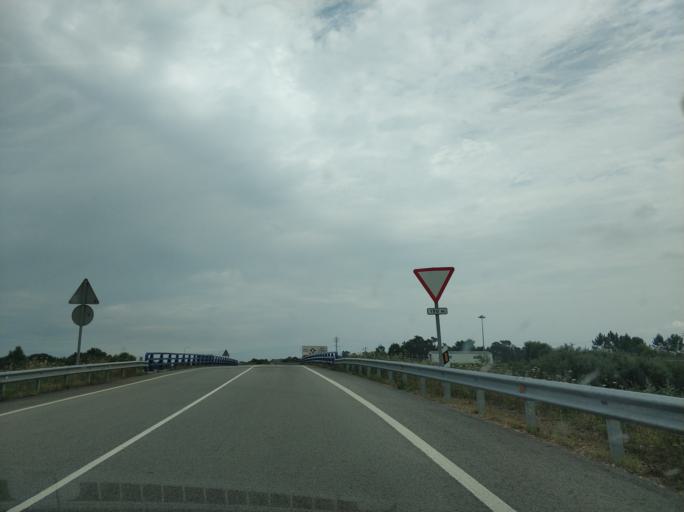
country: ES
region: Asturias
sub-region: Province of Asturias
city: Navia
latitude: 43.5273
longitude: -6.5527
